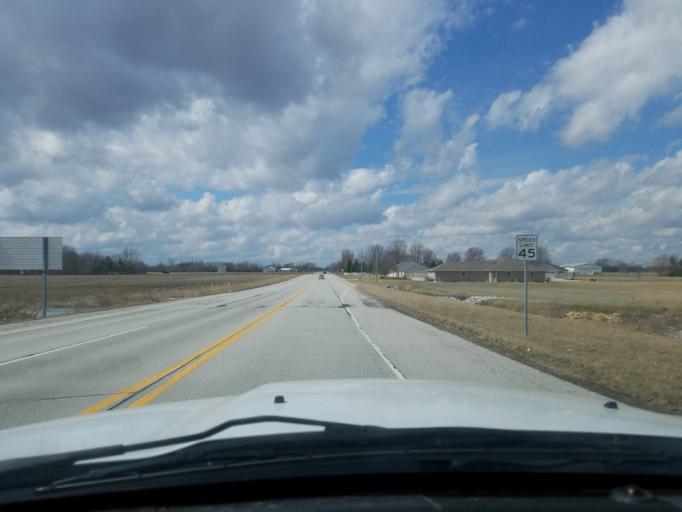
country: US
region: Indiana
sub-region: Howard County
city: Indian Heights
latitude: 40.4629
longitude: -86.0843
